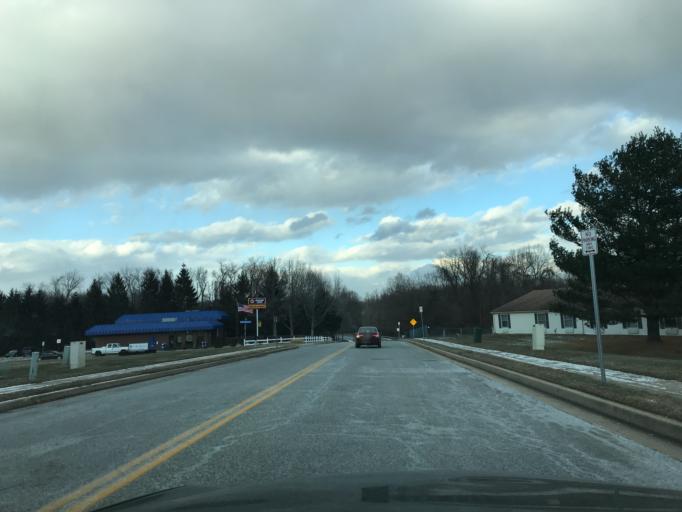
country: US
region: Maryland
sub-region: Harford County
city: Bel Air North
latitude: 39.5713
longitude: -76.3805
